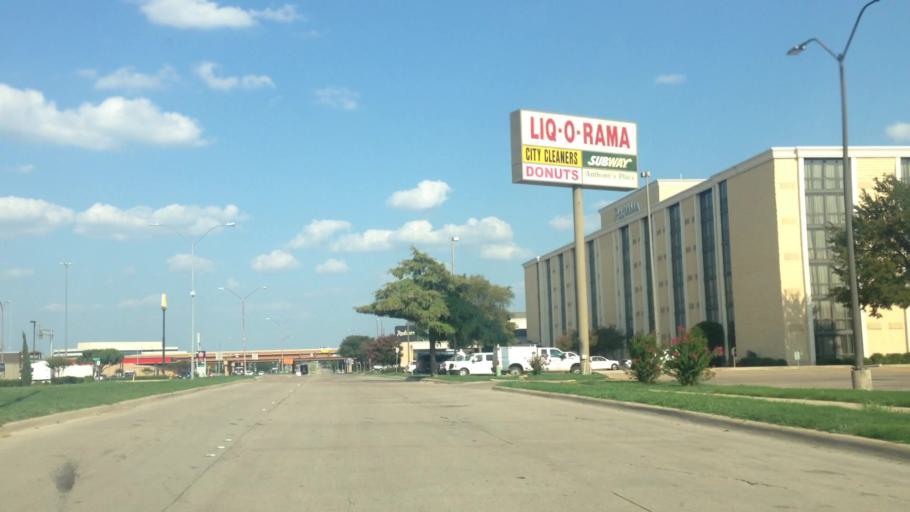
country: US
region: Texas
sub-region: Tarrant County
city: Blue Mound
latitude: 32.8243
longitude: -97.3165
